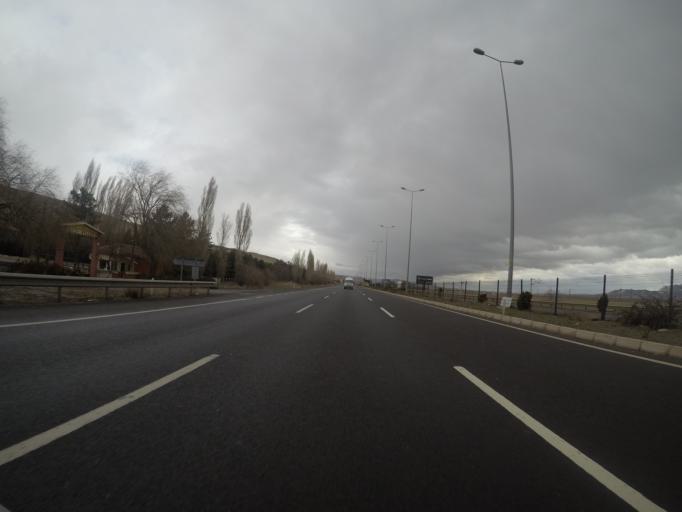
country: TR
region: Kayseri
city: Incesu
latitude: 38.7257
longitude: 35.2780
